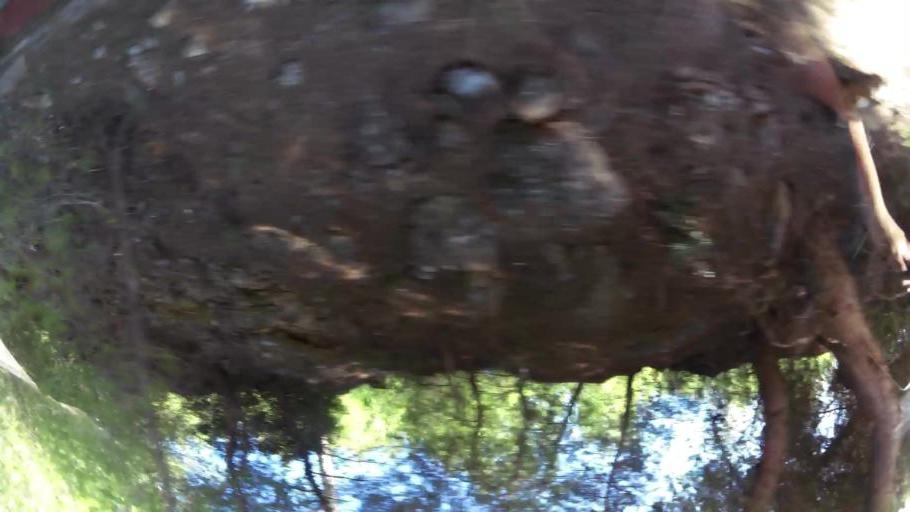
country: GR
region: Attica
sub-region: Nomarchia Anatolikis Attikis
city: Dioni
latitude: 38.0252
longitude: 23.9342
